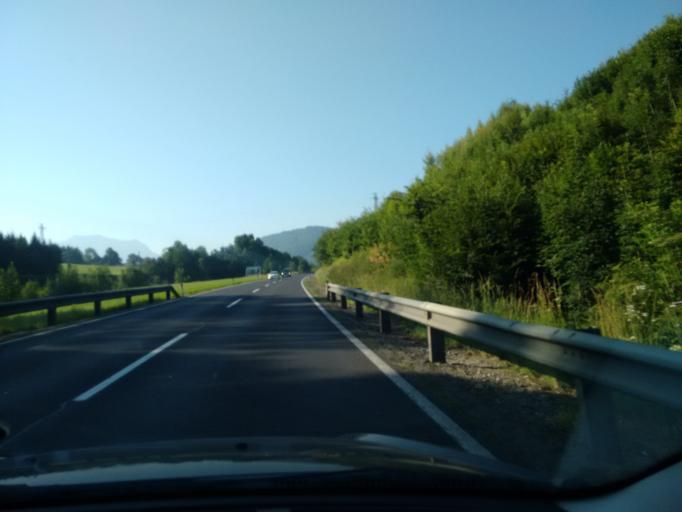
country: AT
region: Upper Austria
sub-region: Politischer Bezirk Gmunden
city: Altmunster
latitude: 47.9446
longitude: 13.7559
